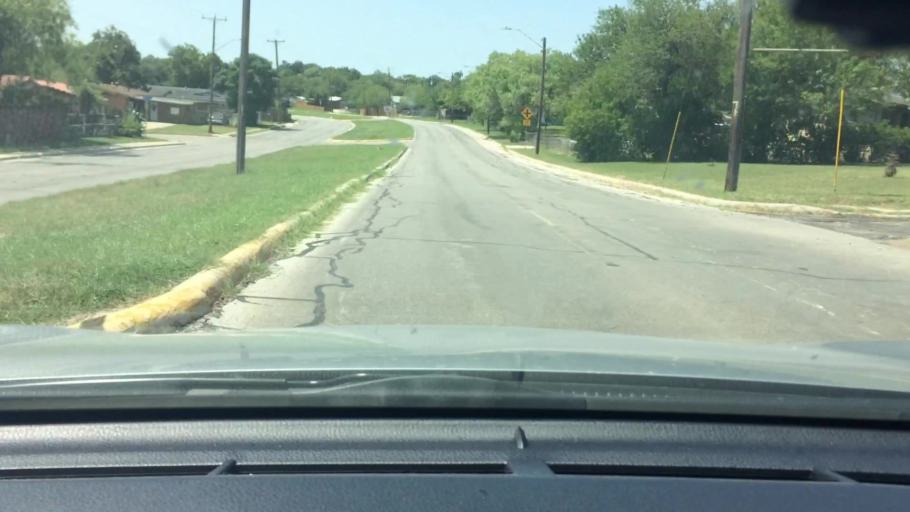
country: US
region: Texas
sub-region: Bexar County
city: San Antonio
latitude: 29.3758
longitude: -98.4338
